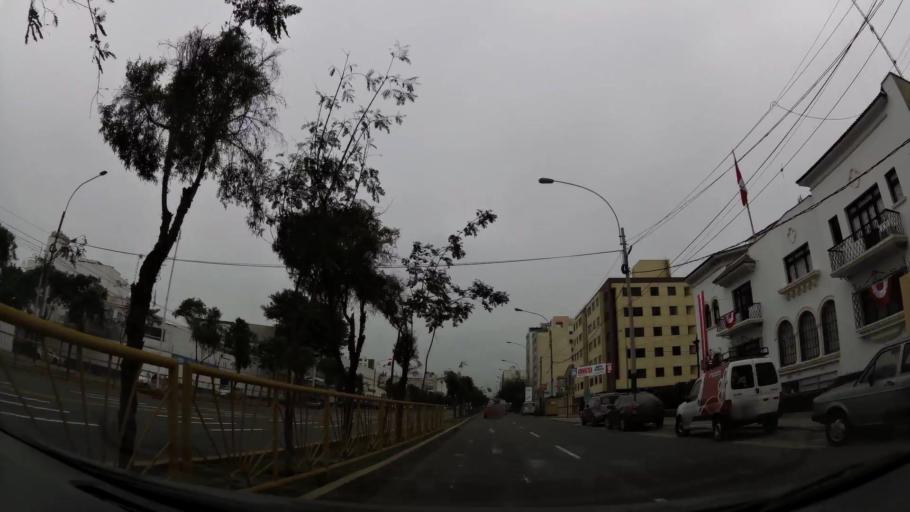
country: PE
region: Lima
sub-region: Lima
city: San Isidro
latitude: -12.0917
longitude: -77.0674
